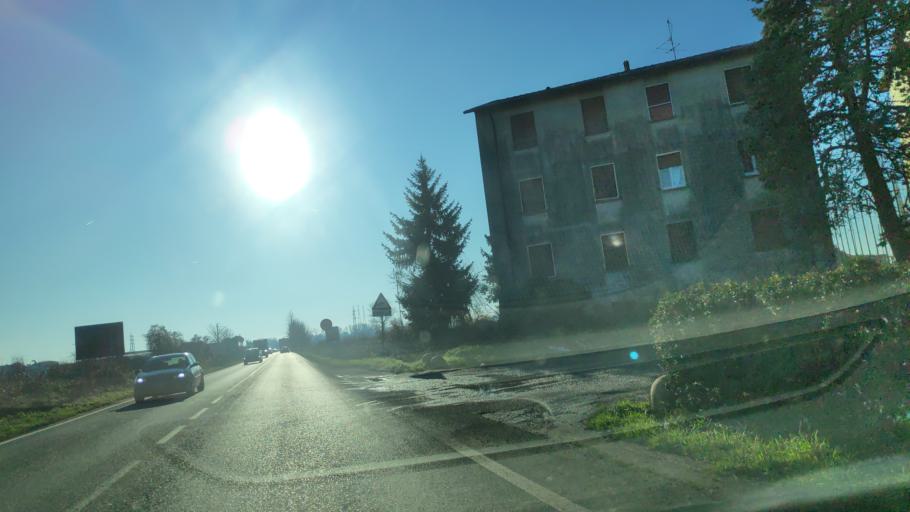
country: IT
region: Lombardy
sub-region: Citta metropolitana di Milano
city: Colturano
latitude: 45.3787
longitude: 9.3395
